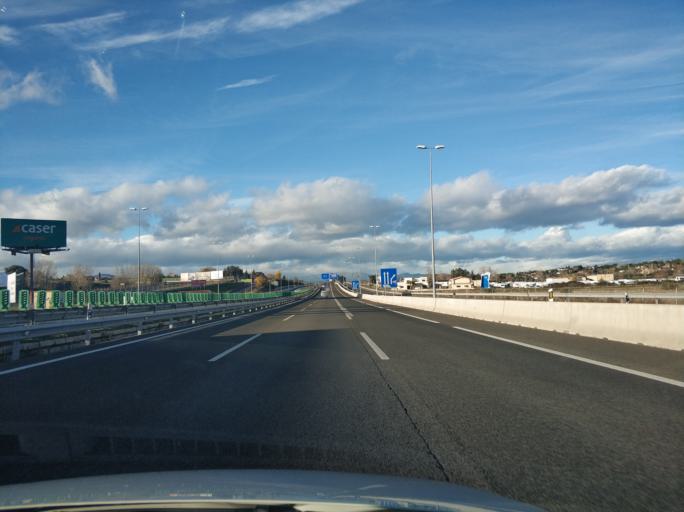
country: ES
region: Madrid
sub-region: Provincia de Madrid
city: San Agustin de Guadalix
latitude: 40.6169
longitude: -3.5830
